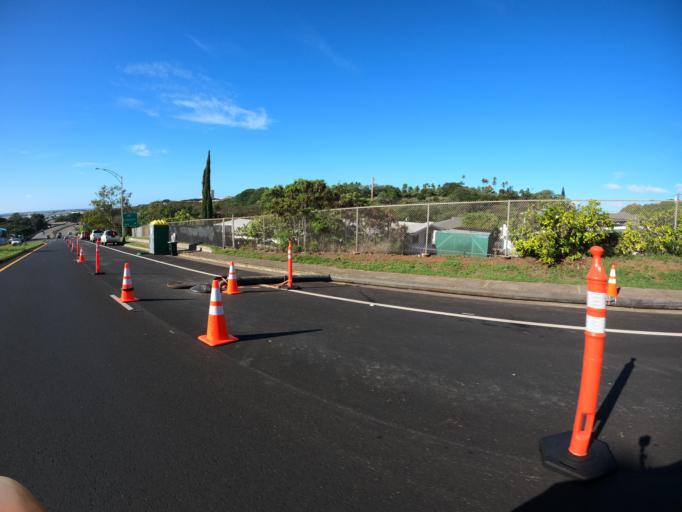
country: US
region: Hawaii
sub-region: Honolulu County
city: Halawa Heights
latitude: 21.3527
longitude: -157.8939
